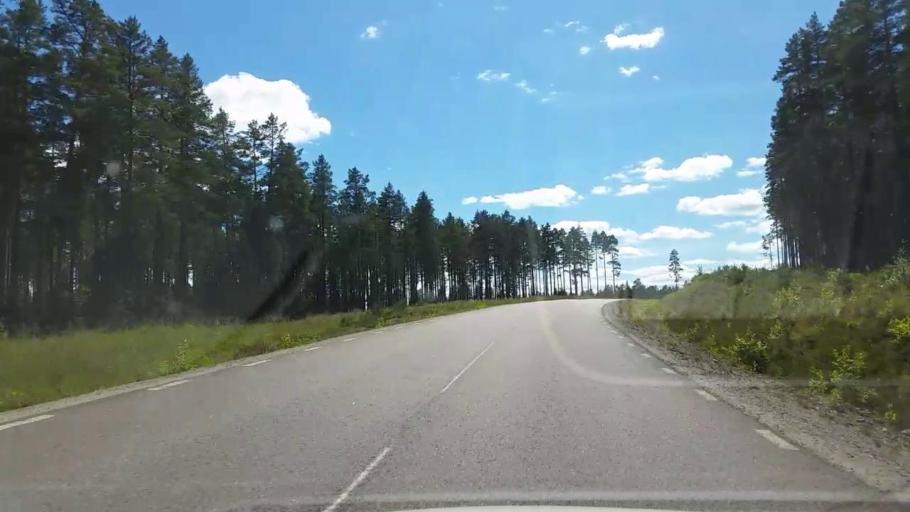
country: SE
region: Dalarna
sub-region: Faluns Kommun
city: Svardsjo
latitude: 61.0354
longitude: 15.7824
